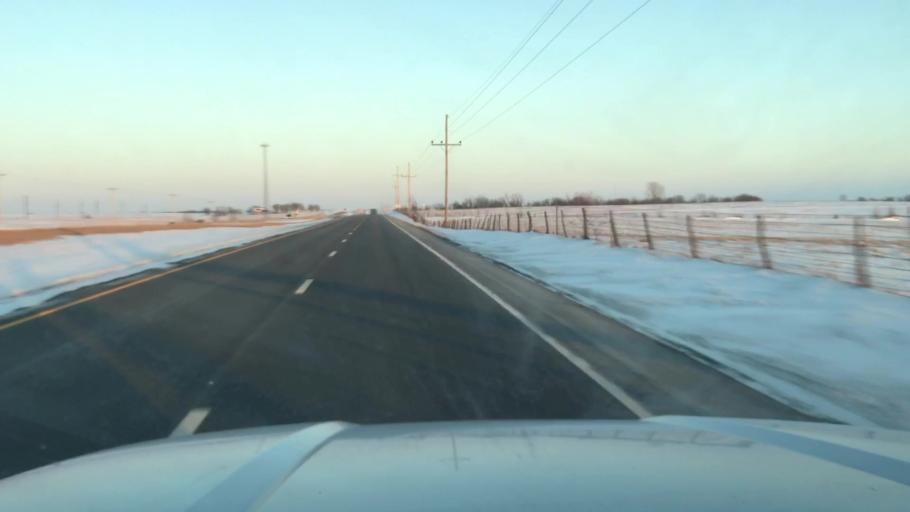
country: US
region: Missouri
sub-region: Clinton County
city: Cameron
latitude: 39.7543
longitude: -94.2912
